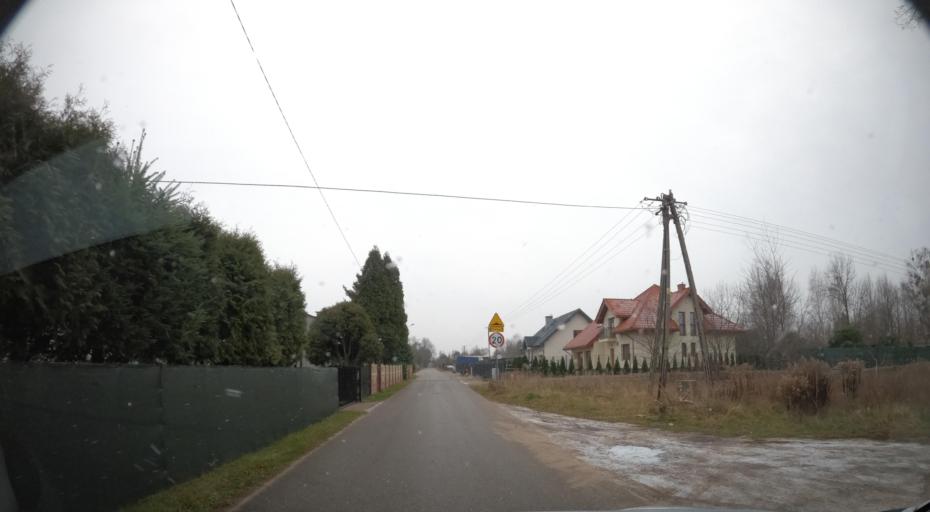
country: PL
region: Masovian Voivodeship
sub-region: Powiat radomski
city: Jastrzebia
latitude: 51.4344
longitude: 21.2277
